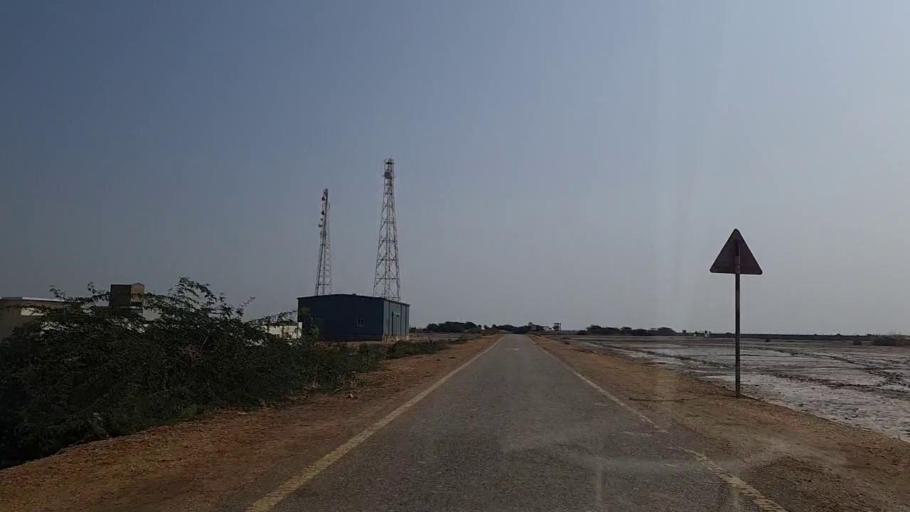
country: PK
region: Sindh
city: Chuhar Jamali
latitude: 24.1658
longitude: 67.8989
